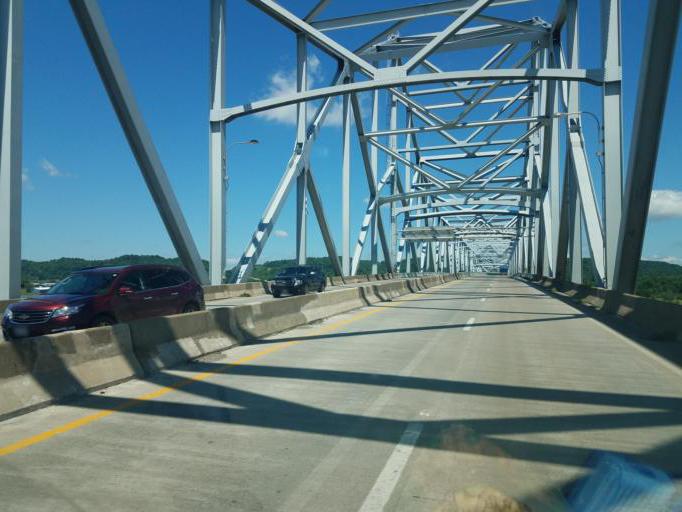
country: US
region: West Virginia
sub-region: Mason County
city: Point Pleasant
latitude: 38.8334
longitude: -82.1459
